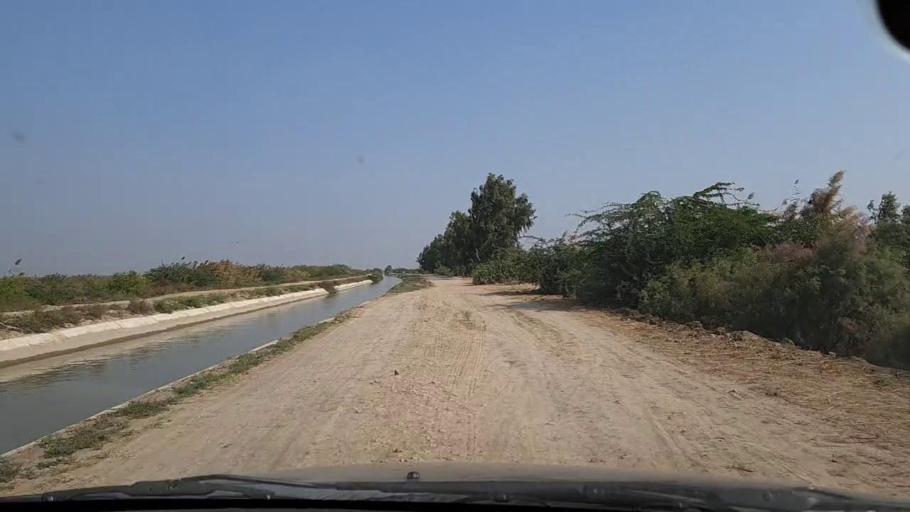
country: PK
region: Sindh
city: Mirpur Sakro
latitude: 24.3420
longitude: 67.7050
